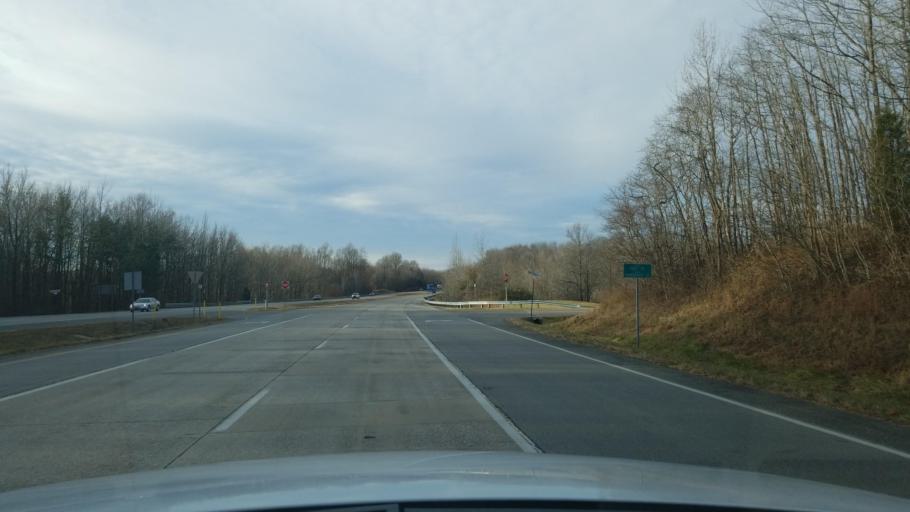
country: US
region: Indiana
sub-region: Vanderburgh County
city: Evansville
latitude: 37.9520
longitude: -87.6989
